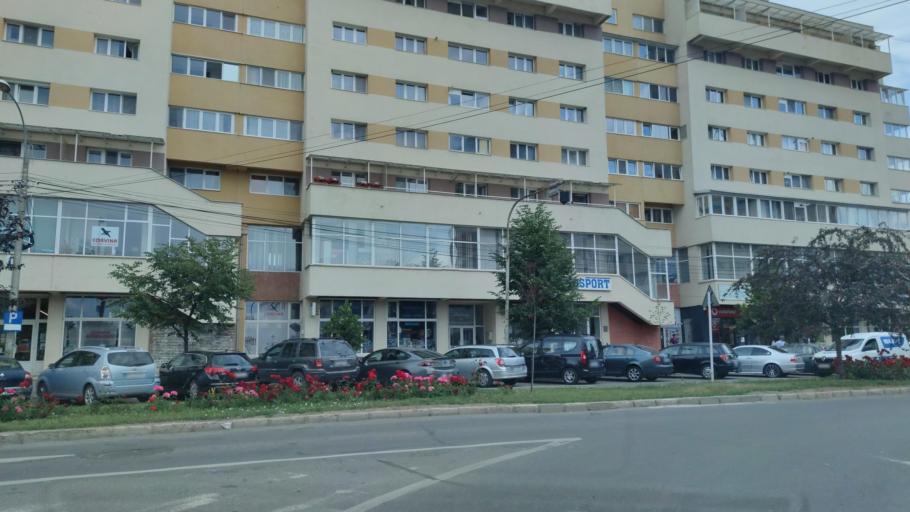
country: RO
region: Harghita
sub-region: Municipiul Miercurea Ciuc
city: Miercurea-Ciuc
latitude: 46.3616
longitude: 25.7990
